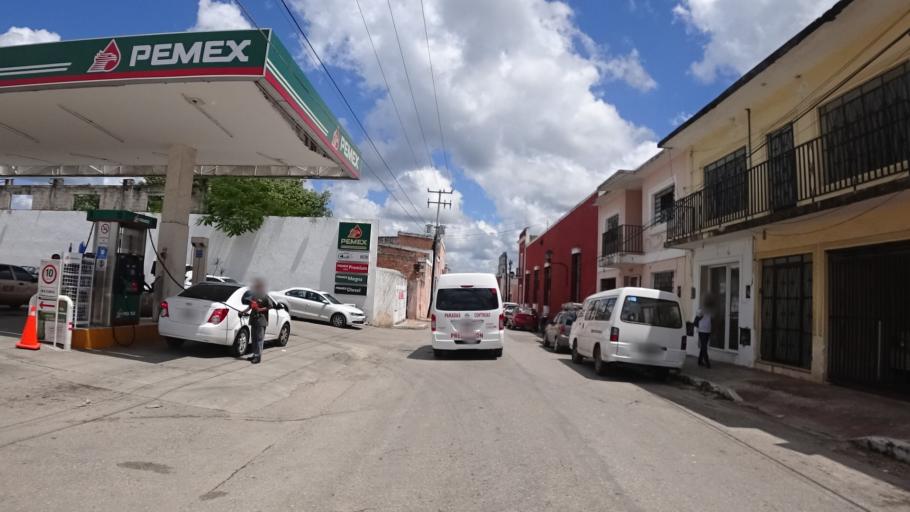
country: MX
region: Yucatan
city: Valladolid
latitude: 20.6897
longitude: -88.2057
